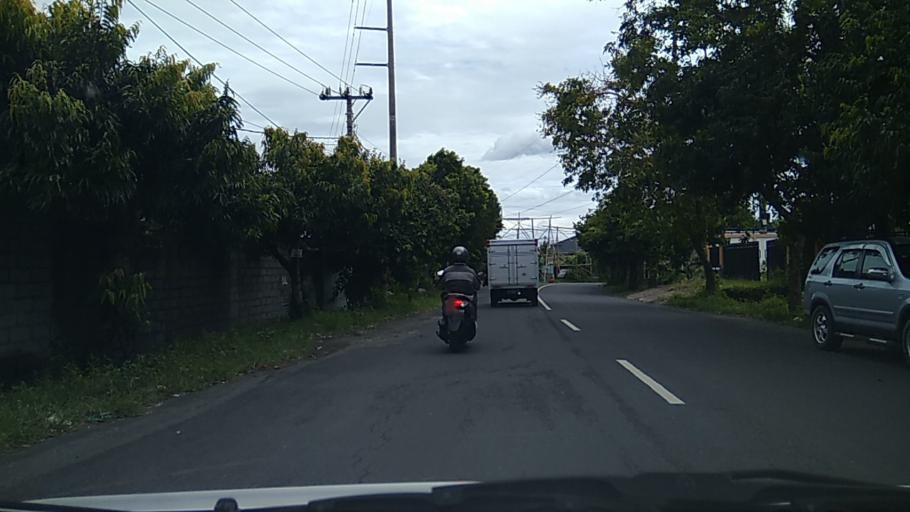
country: ID
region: Bali
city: Banjar Kertajiwa
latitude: -8.6575
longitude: 115.2579
